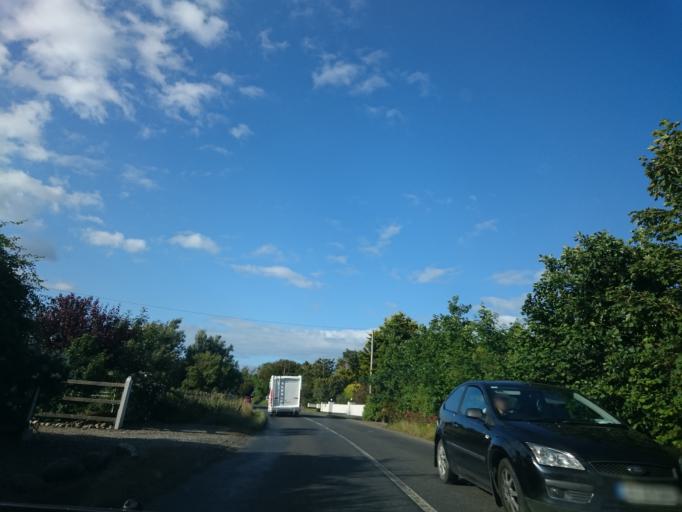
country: IE
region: Leinster
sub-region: Loch Garman
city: Loch Garman
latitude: 52.2005
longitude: -6.5539
